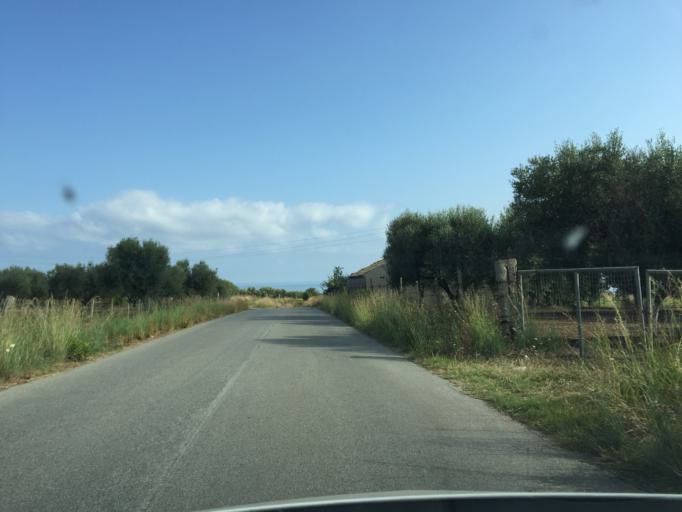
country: IT
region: Calabria
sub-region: Provincia di Vibo-Valentia
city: Pannaconi
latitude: 38.7131
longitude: 16.0490
